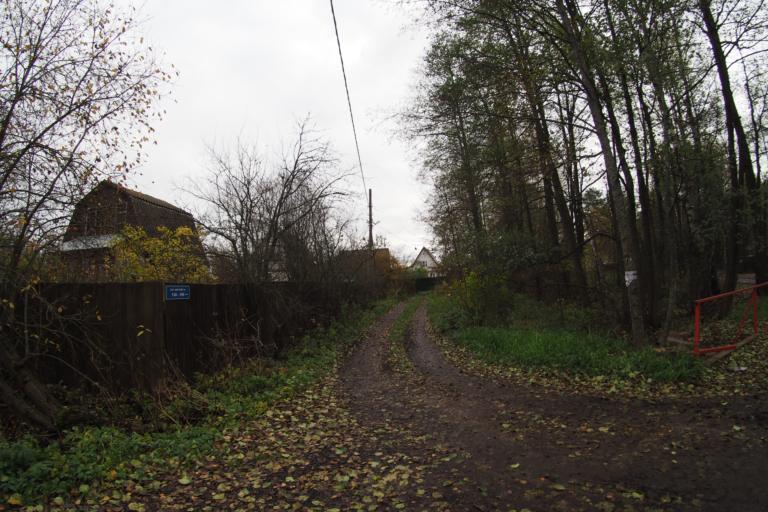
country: RU
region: Moskovskaya
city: Davydovo
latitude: 55.5764
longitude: 38.7581
